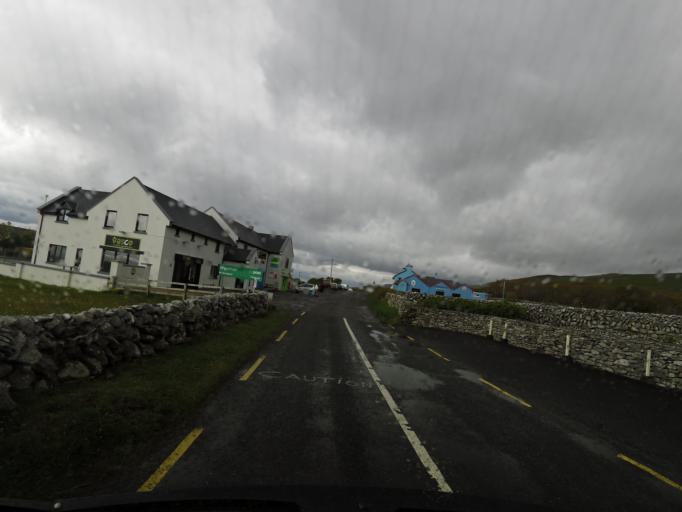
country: IE
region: Connaught
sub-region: County Galway
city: Bearna
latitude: 53.1008
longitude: -9.2976
